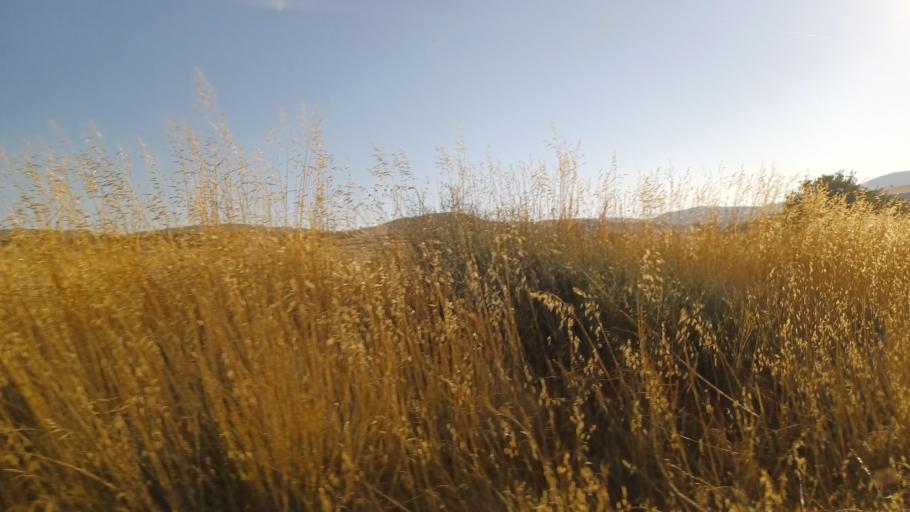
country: CY
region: Larnaka
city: Troulloi
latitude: 35.0233
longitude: 33.6388
